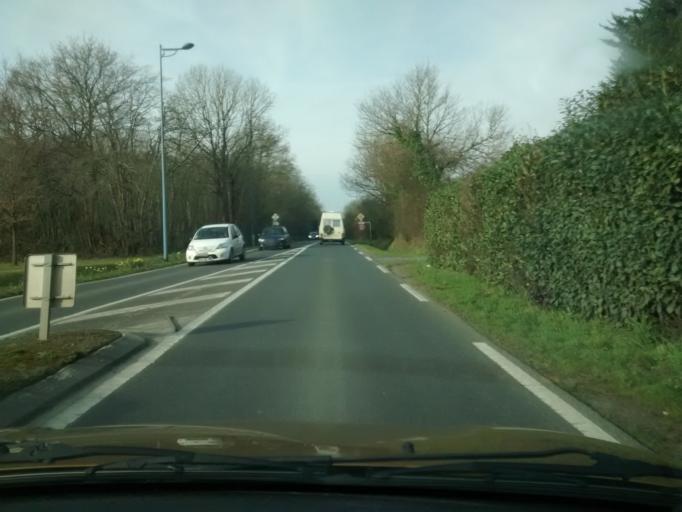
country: FR
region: Pays de la Loire
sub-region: Departement de la Loire-Atlantique
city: Heric
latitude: 47.4151
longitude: -1.6639
